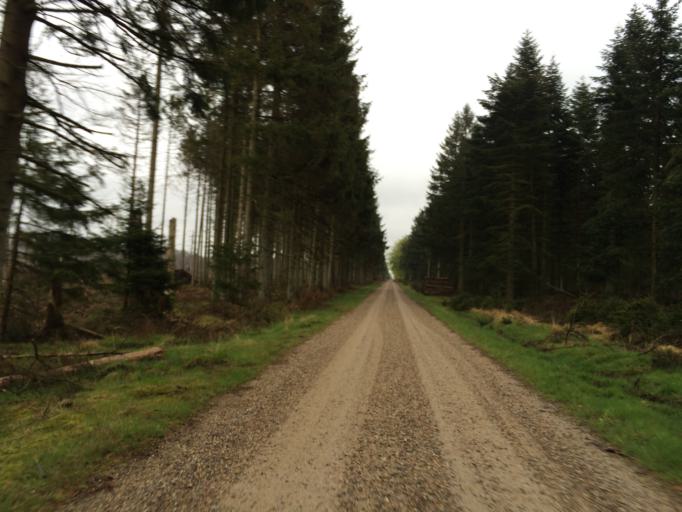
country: DK
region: Central Jutland
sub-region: Holstebro Kommune
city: Ulfborg
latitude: 56.2598
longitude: 8.4451
